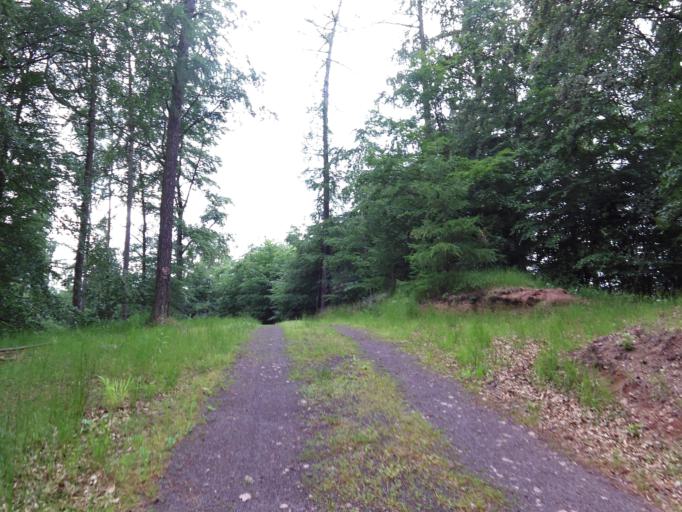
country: DE
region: Thuringia
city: Wolfsburg-Unkeroda
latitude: 50.9259
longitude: 10.3002
